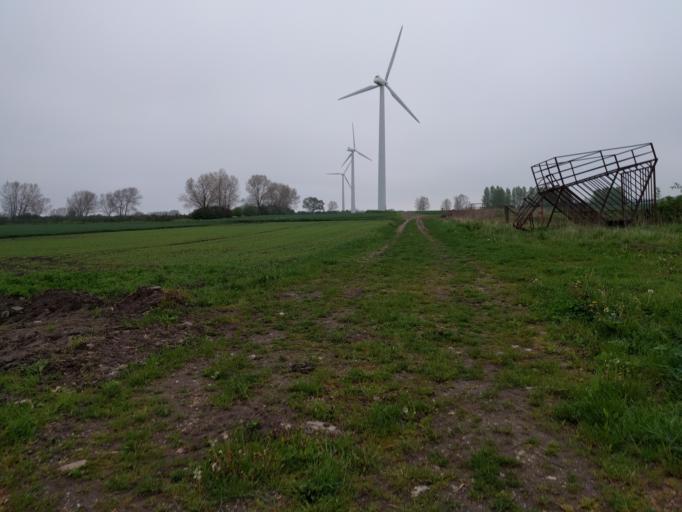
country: DK
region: South Denmark
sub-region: Kerteminde Kommune
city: Langeskov
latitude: 55.3957
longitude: 10.5315
